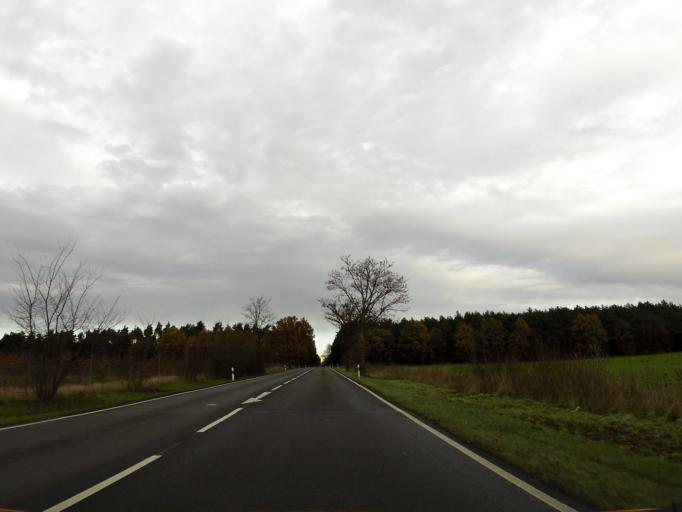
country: DE
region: Saxony-Anhalt
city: Letzlingen
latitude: 52.3794
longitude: 11.4653
